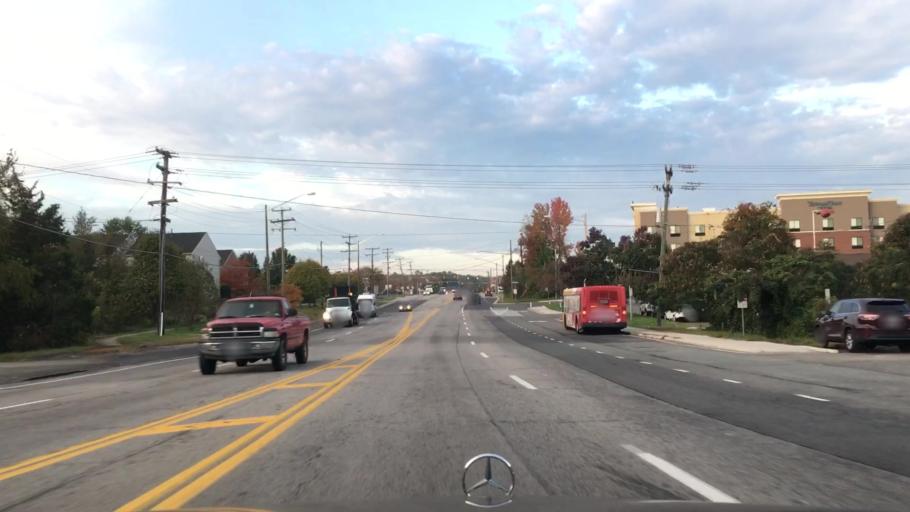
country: US
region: Virginia
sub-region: Fairfax County
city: Woodlawn
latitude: 38.7224
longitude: -77.1216
